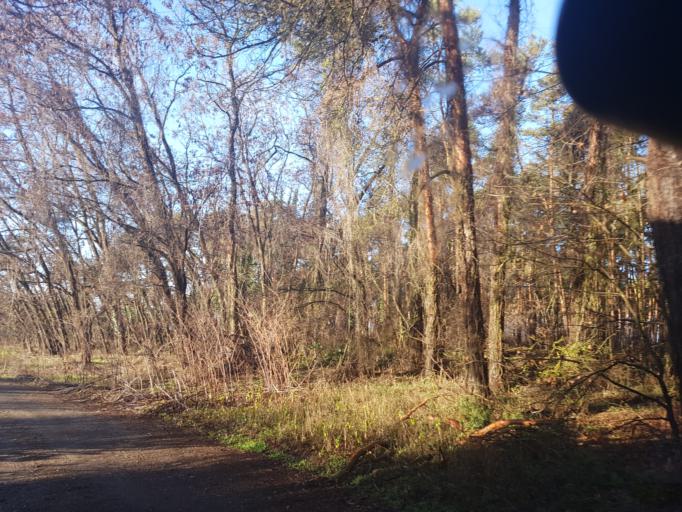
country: DE
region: Brandenburg
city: Trobitz
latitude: 51.5434
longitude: 13.4511
